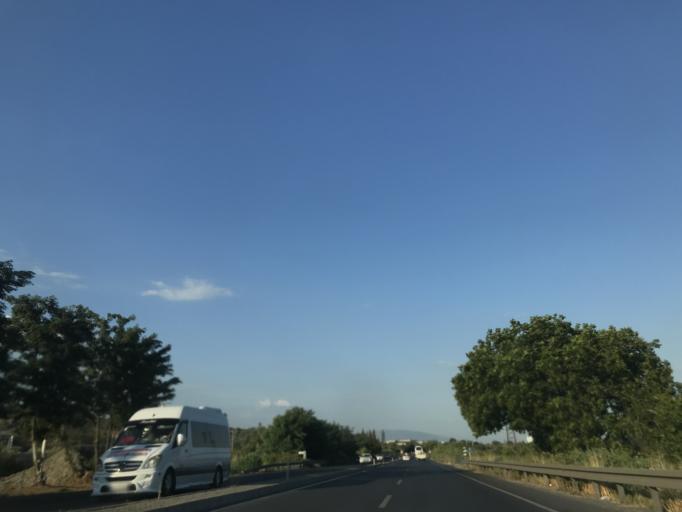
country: TR
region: Aydin
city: Kosk
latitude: 37.8545
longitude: 28.0808
